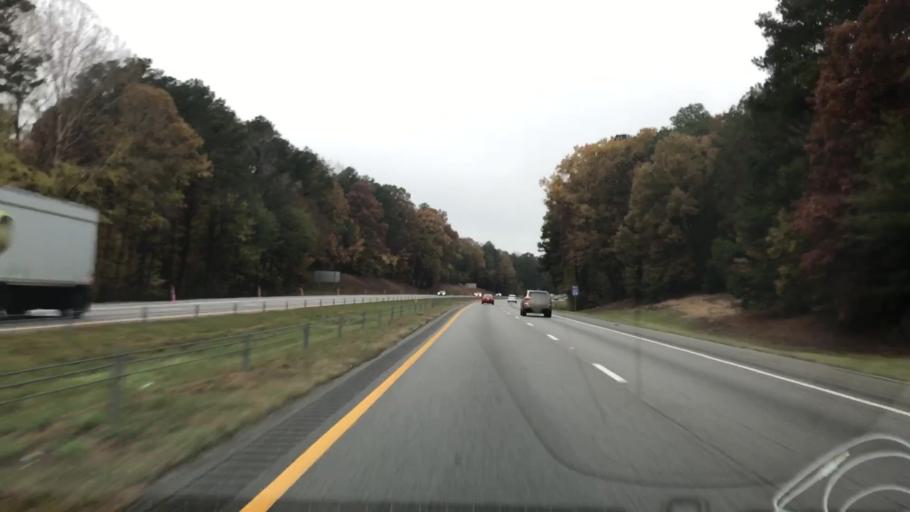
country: US
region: South Carolina
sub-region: Newberry County
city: Prosperity
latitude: 34.2414
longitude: -81.4679
